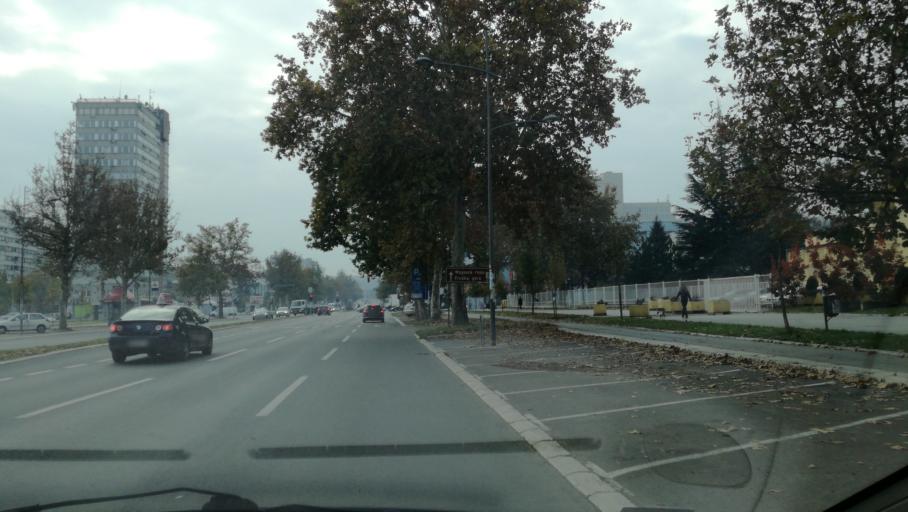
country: RS
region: Autonomna Pokrajina Vojvodina
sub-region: Juznobacki Okrug
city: Novi Sad
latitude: 45.2451
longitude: 19.8406
